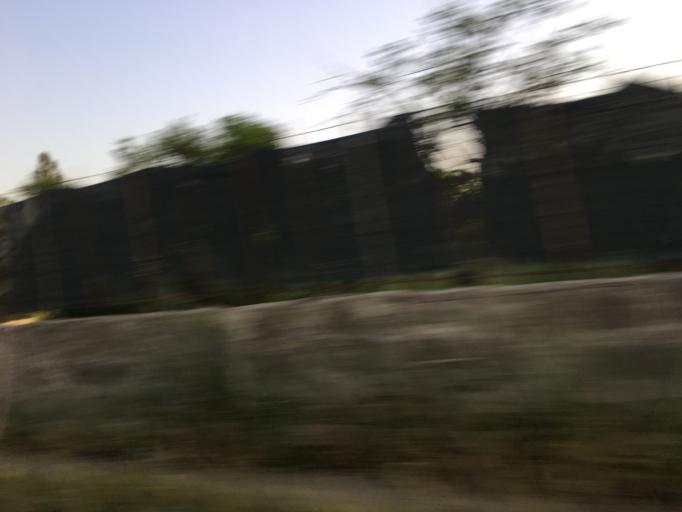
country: IT
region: Apulia
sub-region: Provincia di Lecce
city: San Pietro in Lama
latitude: 40.3053
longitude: 18.1324
